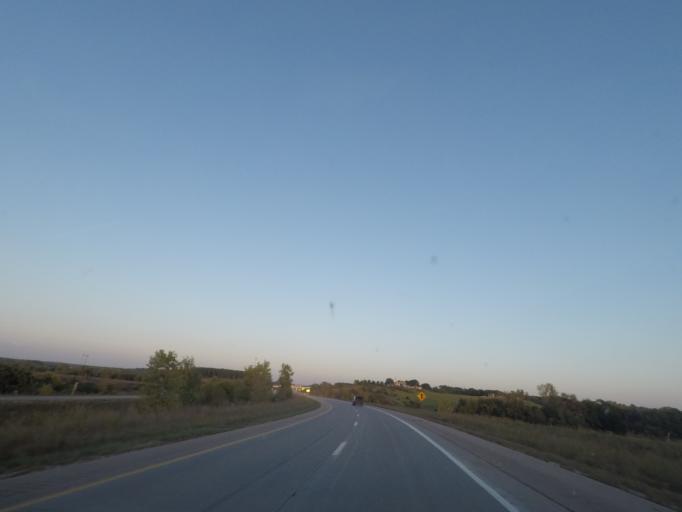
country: US
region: Iowa
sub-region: Polk County
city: West Des Moines
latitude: 41.5227
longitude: -93.7705
